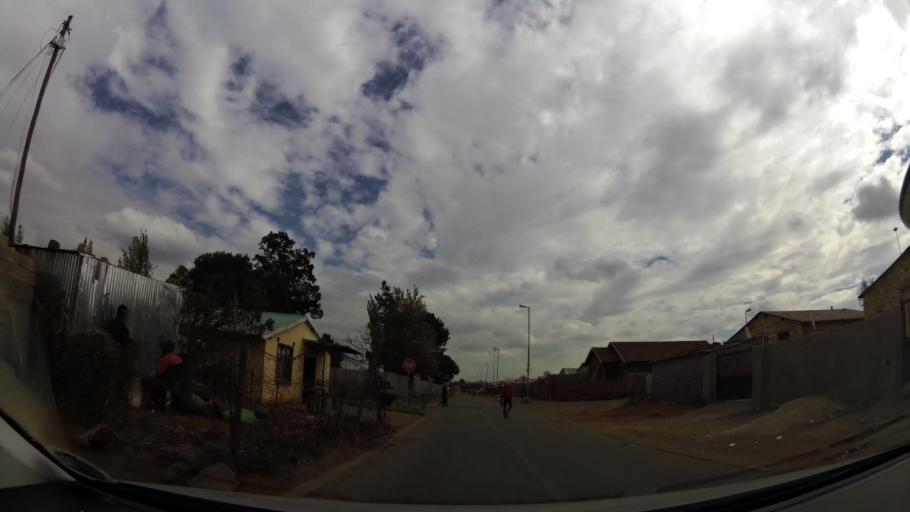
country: ZA
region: Gauteng
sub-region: City of Johannesburg Metropolitan Municipality
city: Soweto
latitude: -26.2804
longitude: 27.8551
